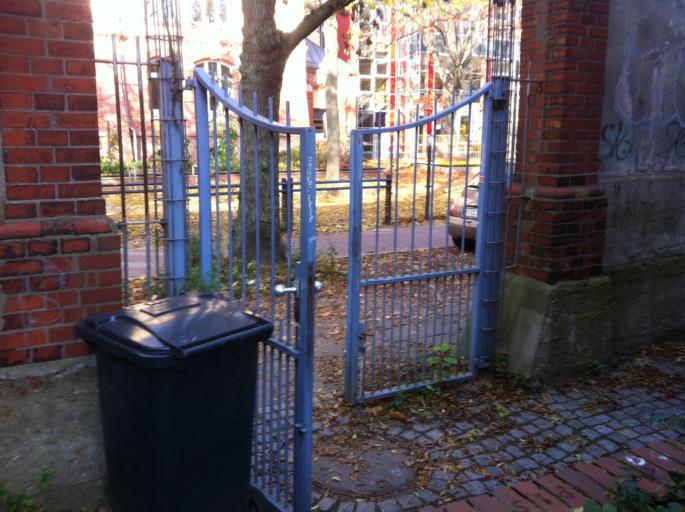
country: DE
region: Hamburg
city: Altona
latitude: 53.5592
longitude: 9.9418
